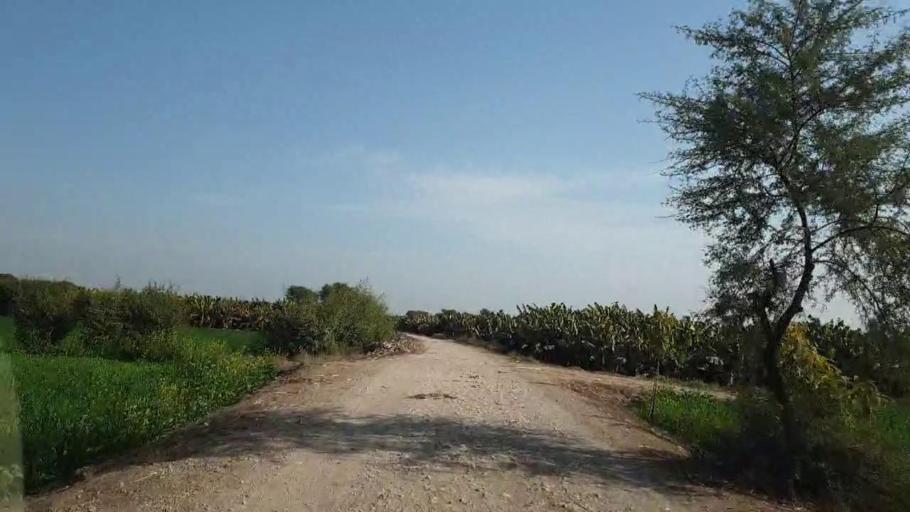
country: PK
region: Sindh
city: Tando Allahyar
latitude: 25.5789
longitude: 68.6080
